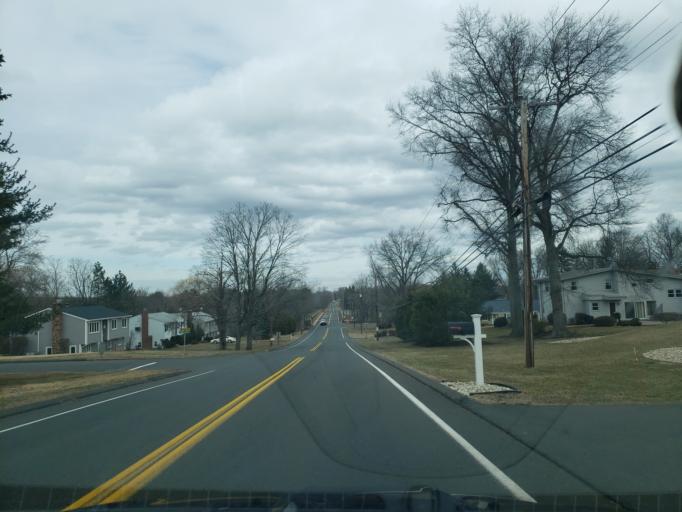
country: US
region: Connecticut
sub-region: Hartford County
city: Wethersfield
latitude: 41.6637
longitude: -72.6653
